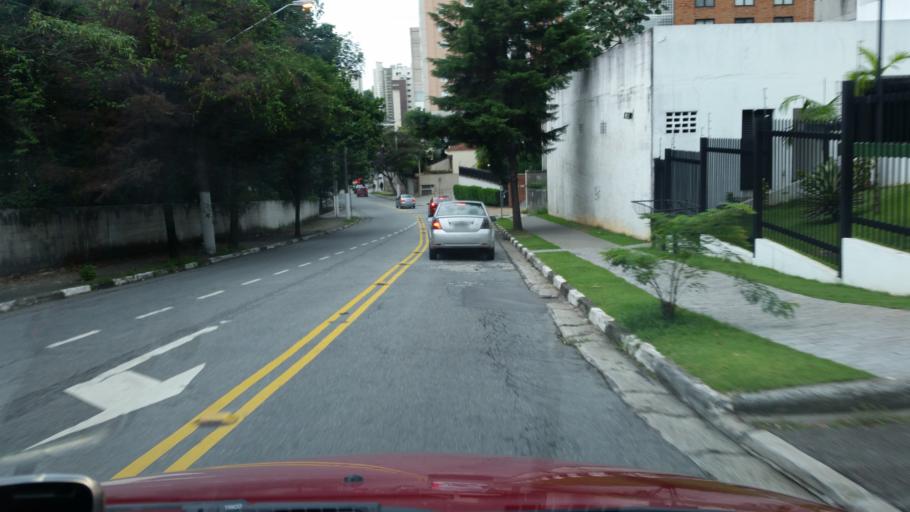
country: BR
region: Sao Paulo
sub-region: Taboao Da Serra
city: Taboao da Serra
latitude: -23.6308
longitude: -46.7346
